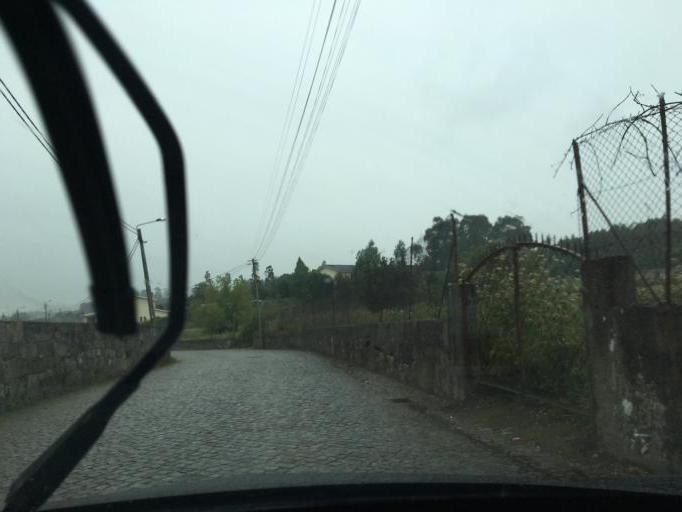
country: PT
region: Porto
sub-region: Maia
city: Anta
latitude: 41.2759
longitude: -8.6178
